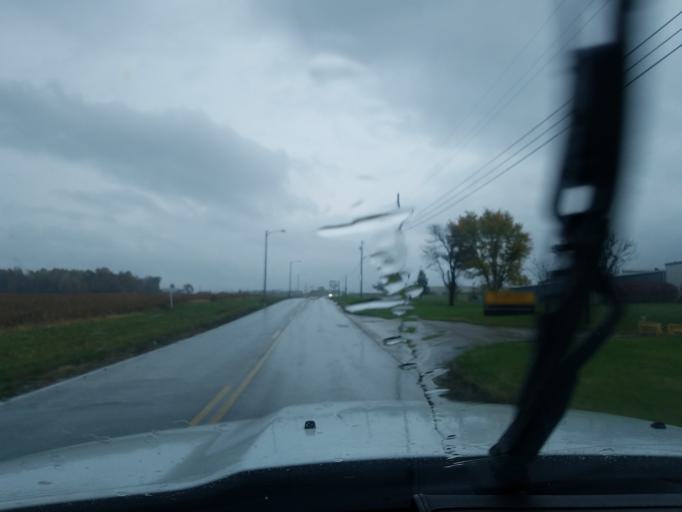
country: US
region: Kentucky
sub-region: Taylor County
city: Campbellsville
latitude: 37.3474
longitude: -85.3282
